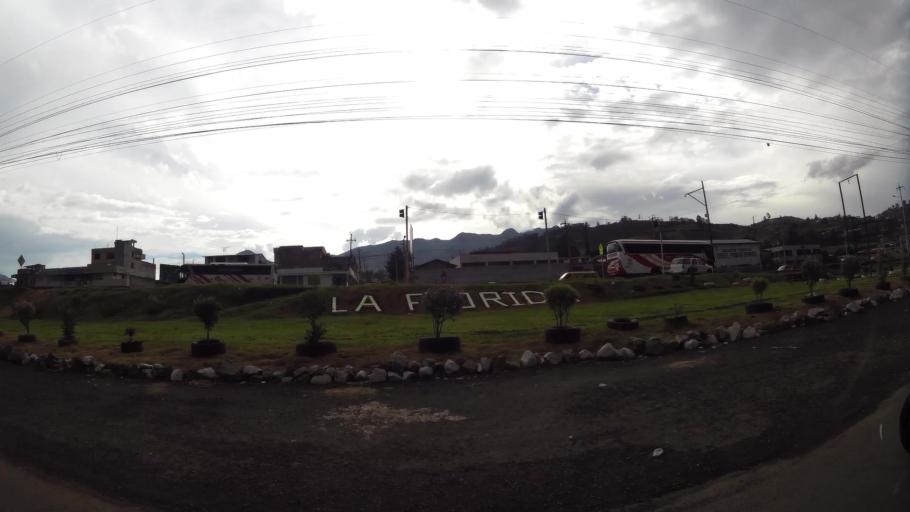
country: EC
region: Pichincha
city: Machachi
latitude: -0.4114
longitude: -78.5474
